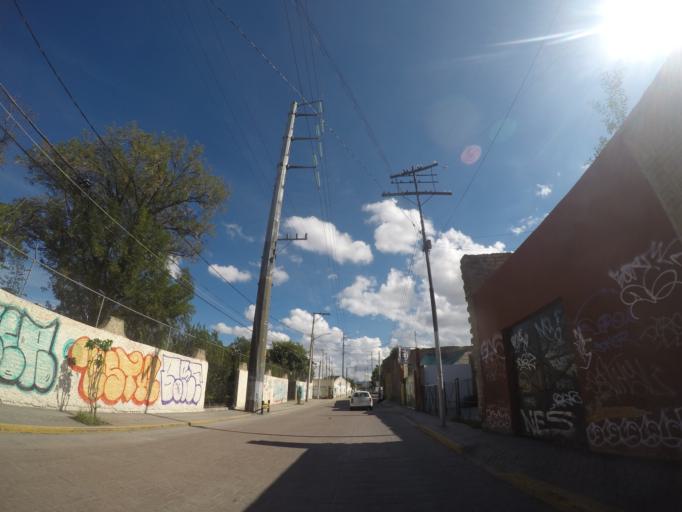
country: MX
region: San Luis Potosi
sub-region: San Luis Potosi
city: San Luis Potosi
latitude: 22.1551
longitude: -100.9680
